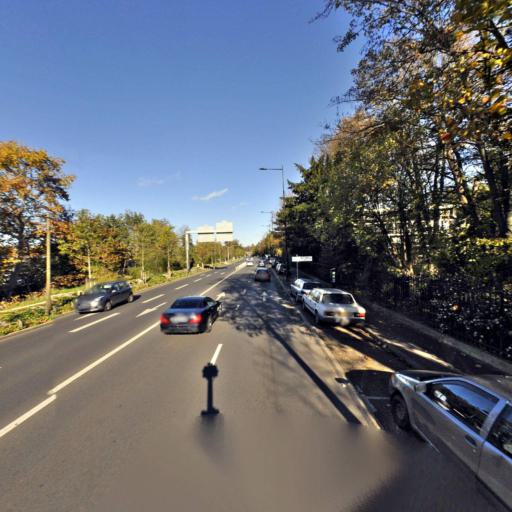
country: FR
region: Ile-de-France
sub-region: Departement des Hauts-de-Seine
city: Sevres
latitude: 48.8442
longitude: 2.2263
